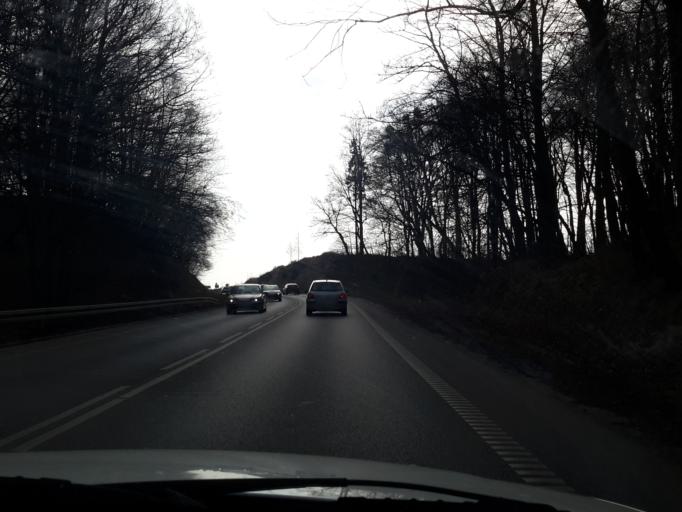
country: PL
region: Pomeranian Voivodeship
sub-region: Powiat wejherowski
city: Rekowo Dolne
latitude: 54.6592
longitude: 18.3618
